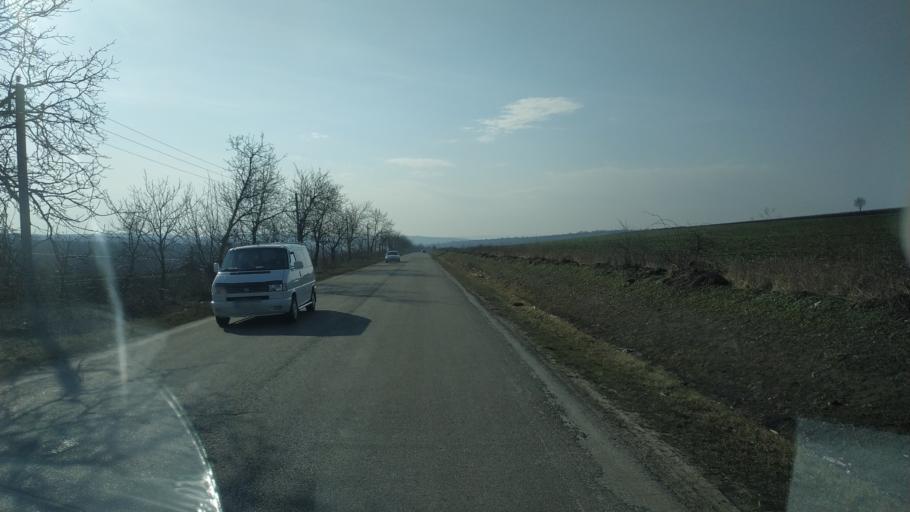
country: MD
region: Chisinau
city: Singera
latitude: 46.8526
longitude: 29.0223
